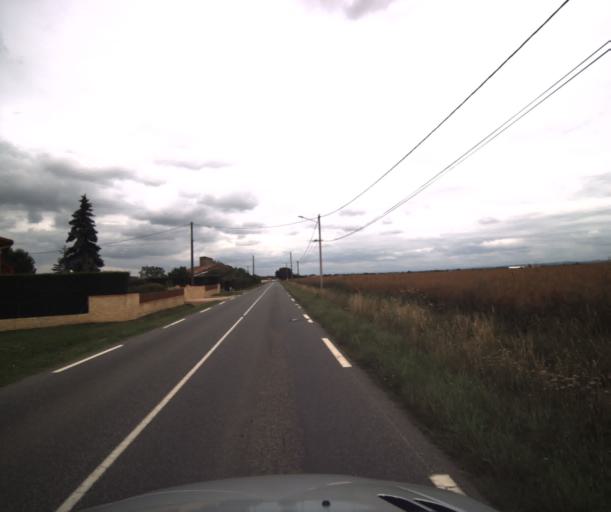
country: FR
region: Midi-Pyrenees
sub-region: Departement de la Haute-Garonne
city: Labarthe-sur-Leze
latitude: 43.4486
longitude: 1.4096
